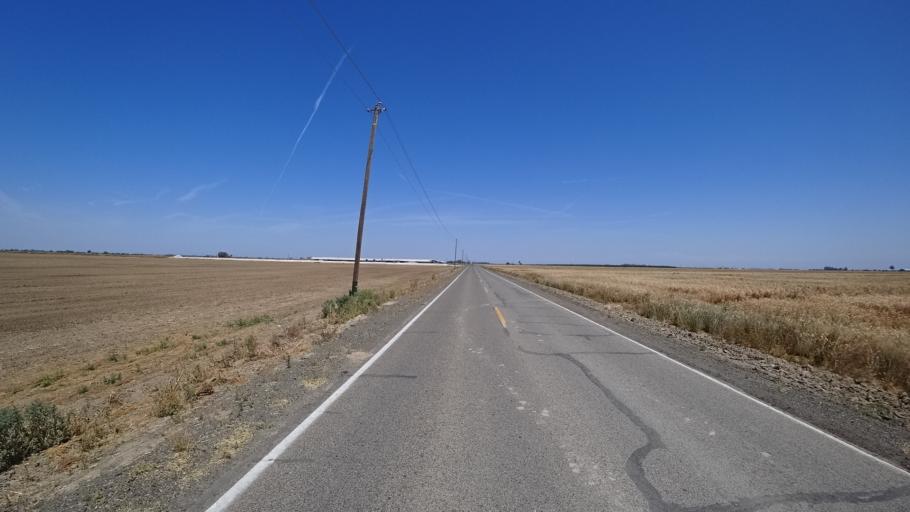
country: US
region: California
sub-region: Kings County
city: Armona
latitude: 36.2140
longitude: -119.7086
